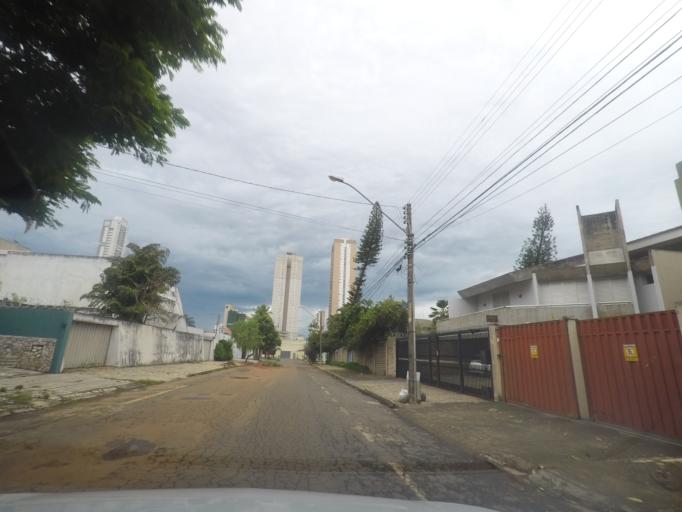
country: BR
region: Goias
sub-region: Goiania
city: Goiania
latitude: -16.6921
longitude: -49.2638
